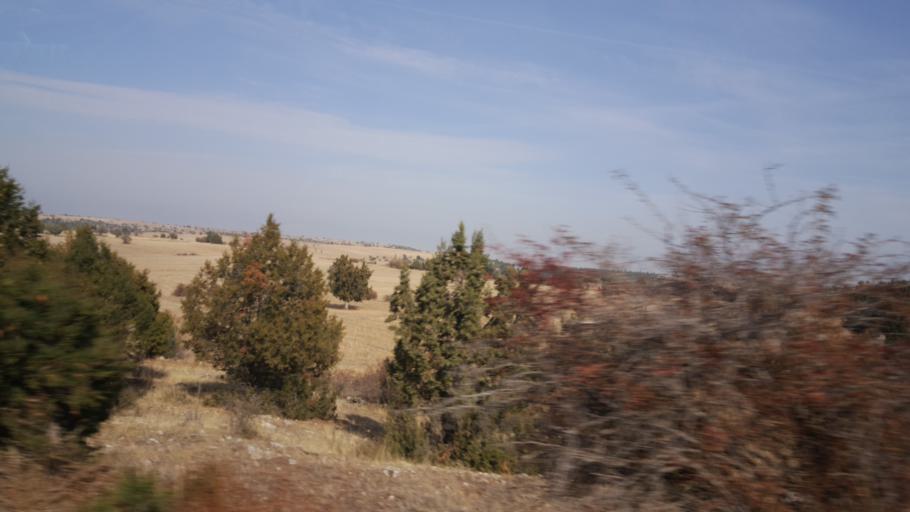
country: TR
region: Eskisehir
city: Mihaliccik
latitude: 39.9596
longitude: 31.3964
